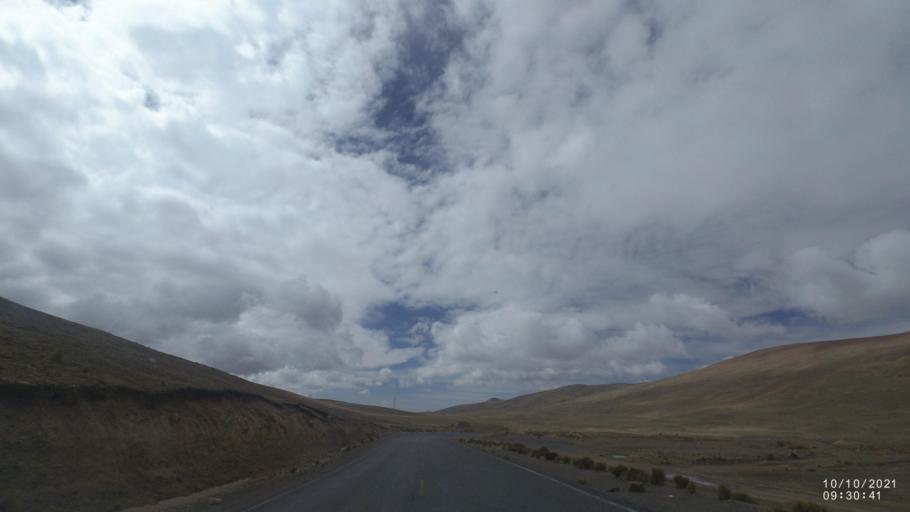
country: BO
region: La Paz
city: Quime
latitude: -17.1214
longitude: -67.3294
